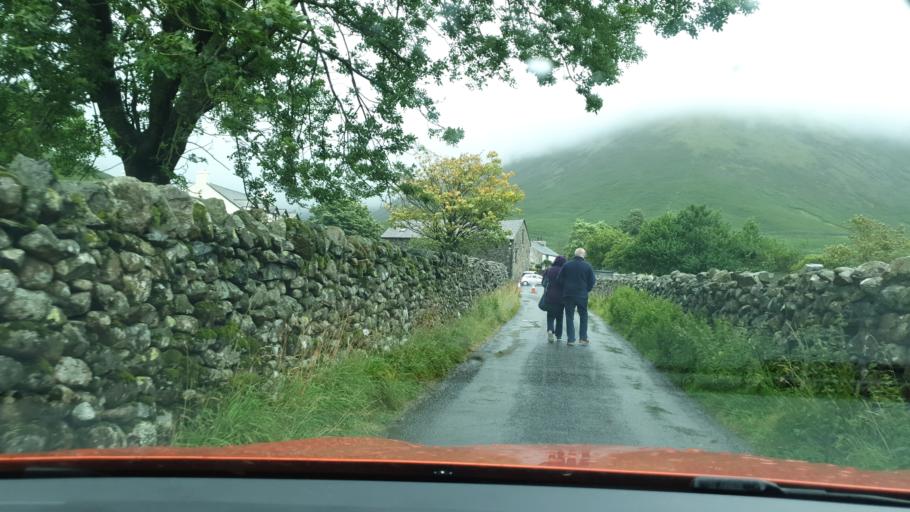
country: GB
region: England
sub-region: Cumbria
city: Keswick
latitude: 54.4669
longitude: -3.2564
